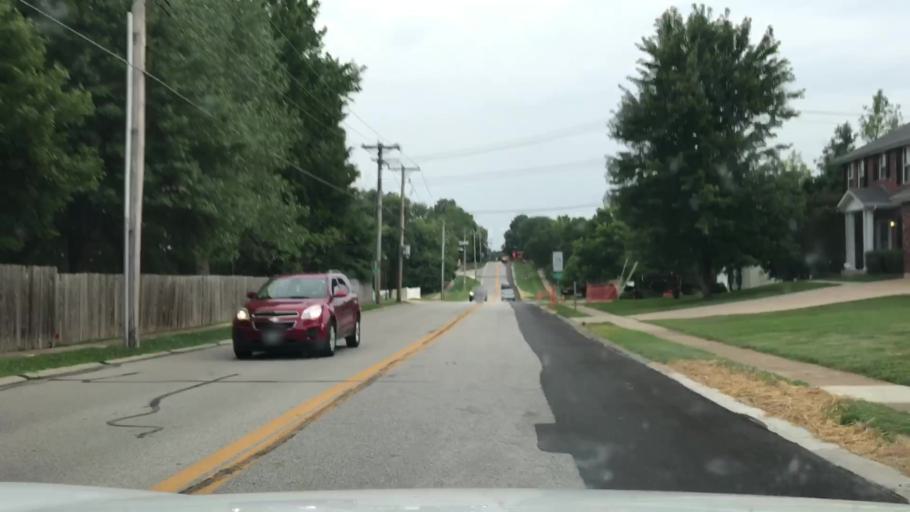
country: US
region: Missouri
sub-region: Saint Louis County
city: Ellisville
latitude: 38.5868
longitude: -90.5671
